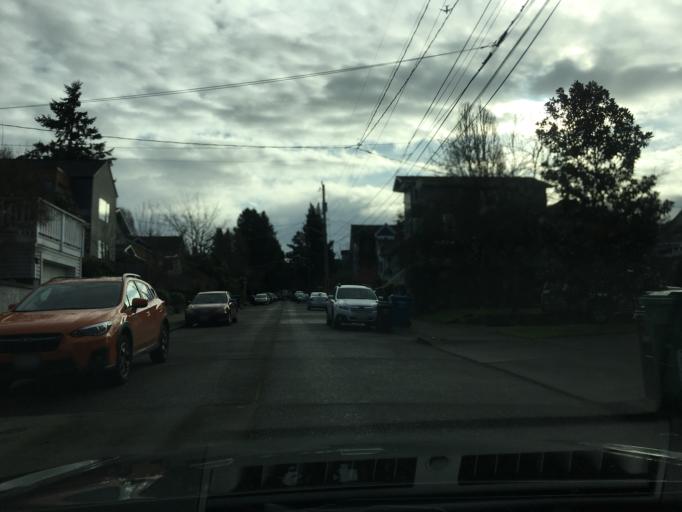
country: US
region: Washington
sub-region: King County
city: Seattle
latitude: 47.6699
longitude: -122.3363
